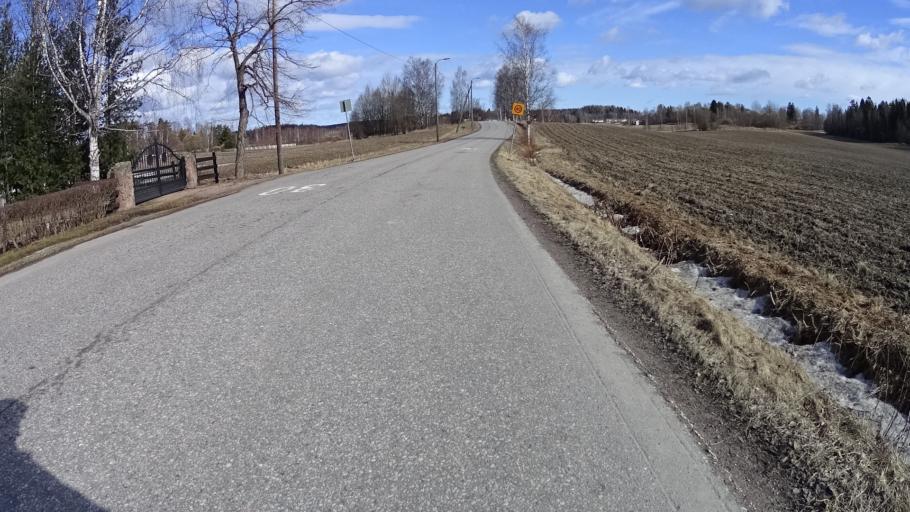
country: FI
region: Uusimaa
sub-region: Helsinki
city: Kilo
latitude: 60.2630
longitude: 24.7721
